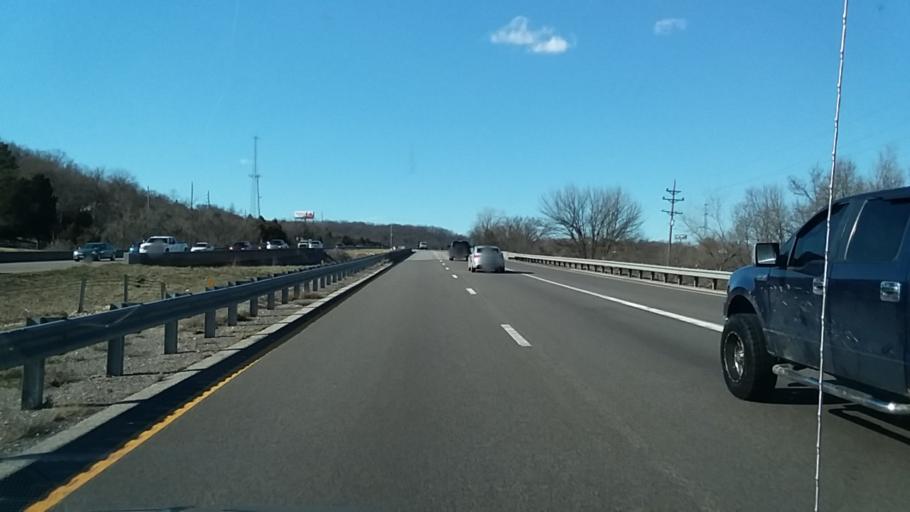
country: US
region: Missouri
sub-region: Jefferson County
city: Pevely
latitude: 38.2911
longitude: -90.4038
